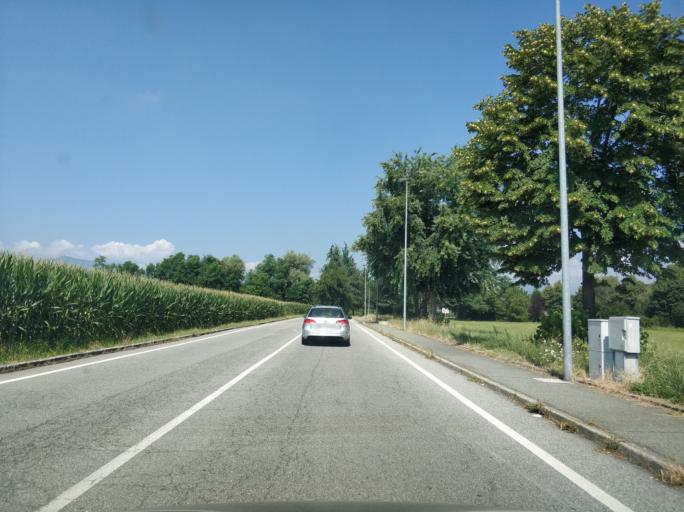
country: IT
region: Piedmont
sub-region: Provincia di Torino
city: San Carlo Canavese
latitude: 45.2379
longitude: 7.6119
